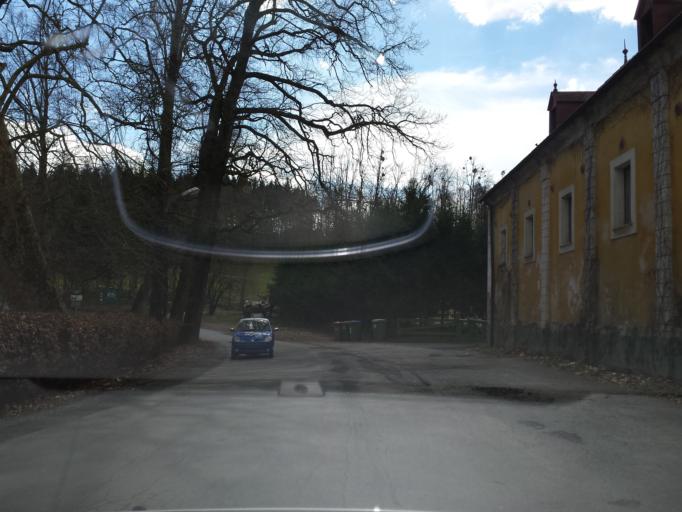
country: AT
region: Styria
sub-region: Politischer Bezirk Deutschlandsberg
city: Deutschlandsberg
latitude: 46.8135
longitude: 15.2434
